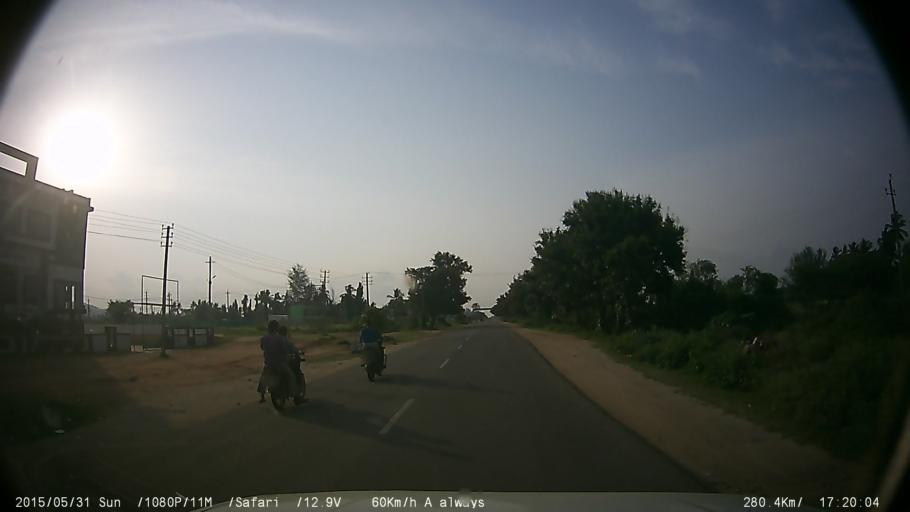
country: IN
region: Karnataka
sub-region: Chamrajnagar
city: Gundlupet
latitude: 11.8200
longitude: 76.6827
